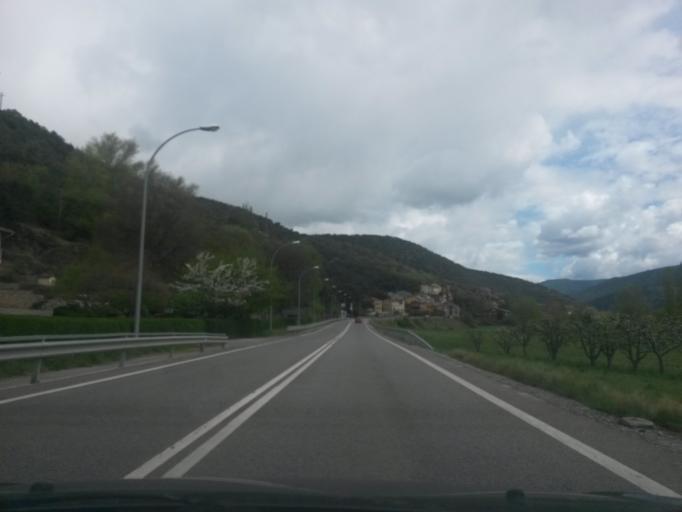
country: ES
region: Catalonia
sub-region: Provincia de Lleida
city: la Seu d'Urgell
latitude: 42.3613
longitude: 1.4762
